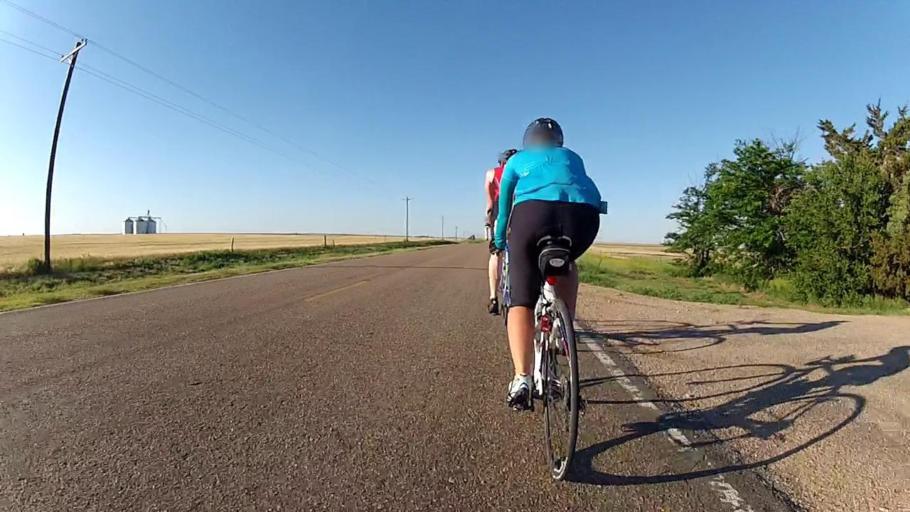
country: US
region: Kansas
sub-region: Ford County
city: Dodge City
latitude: 37.6544
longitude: -99.9070
